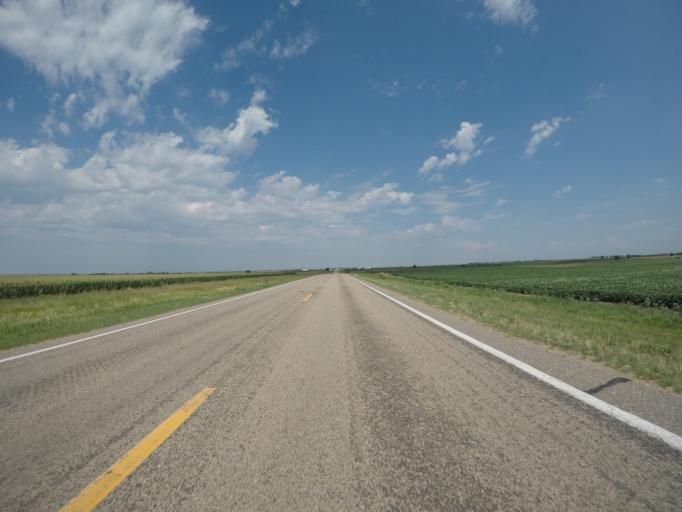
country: US
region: Nebraska
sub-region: Thayer County
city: Hebron
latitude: 40.0166
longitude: -97.7439
